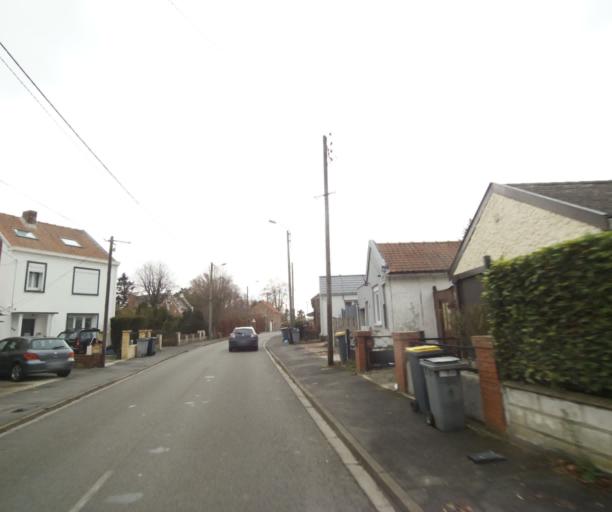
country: FR
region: Nord-Pas-de-Calais
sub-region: Departement du Nord
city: Saint-Saulve
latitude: 50.3625
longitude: 3.5504
